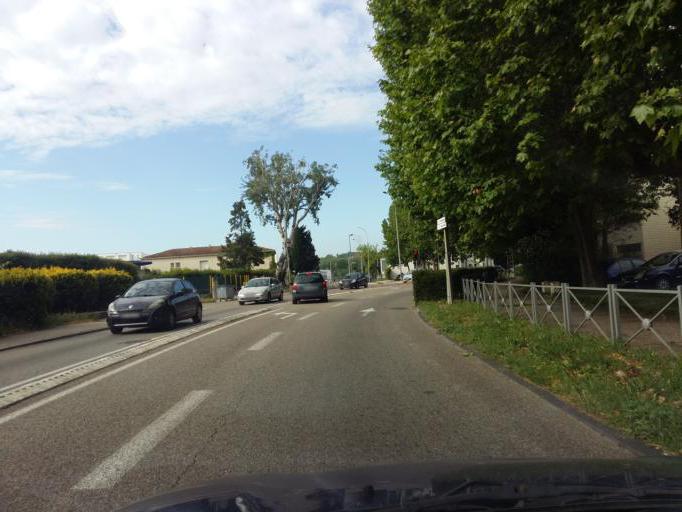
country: FR
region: Languedoc-Roussillon
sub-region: Departement du Gard
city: Bagnols-sur-Ceze
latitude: 44.1562
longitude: 4.6223
